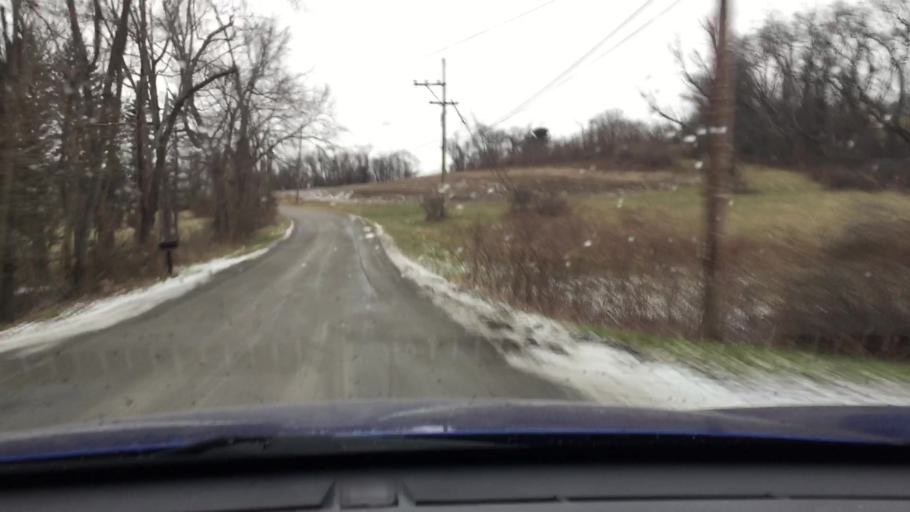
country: US
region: Pennsylvania
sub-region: Westmoreland County
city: Fellsburg
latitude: 40.1628
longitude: -79.8287
